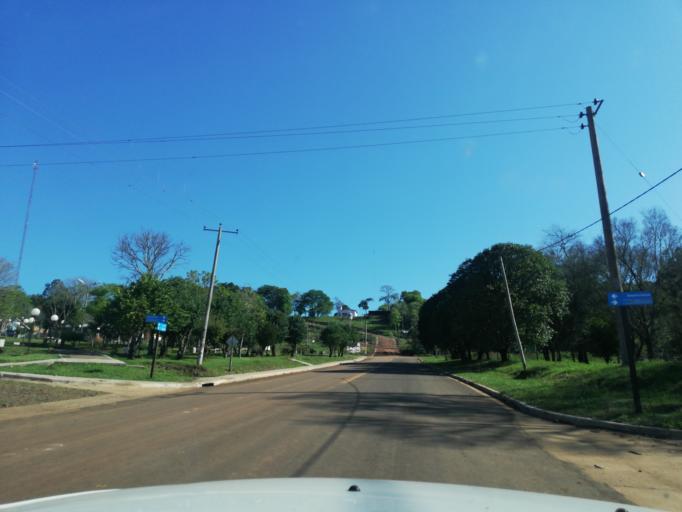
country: AR
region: Misiones
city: Arroyo del Medio
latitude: -27.6975
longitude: -55.4049
